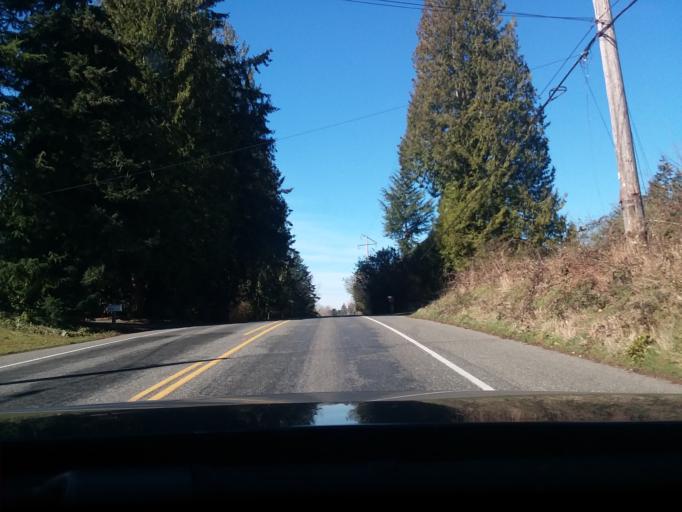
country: US
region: Washington
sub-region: Pierce County
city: Summit
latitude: 47.1619
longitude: -122.3455
